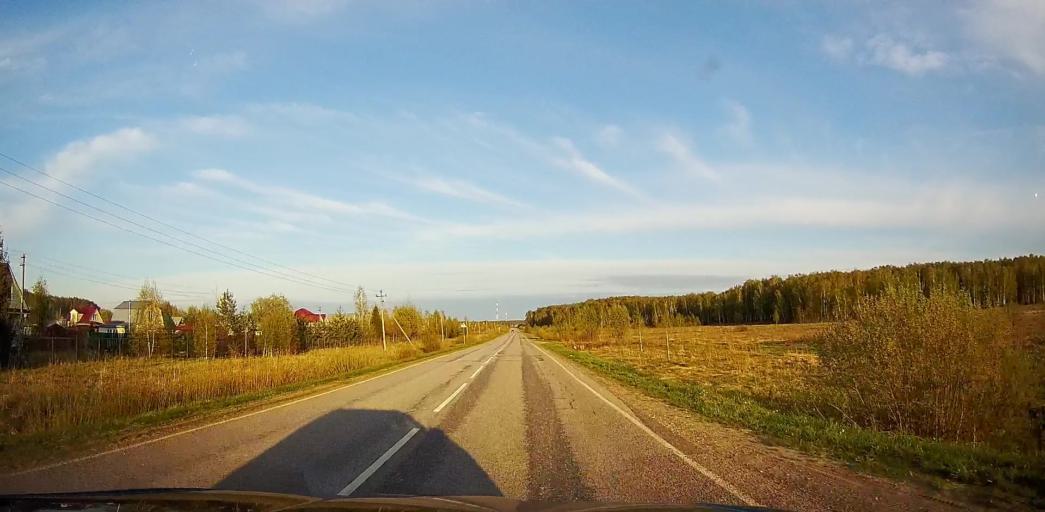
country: RU
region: Moskovskaya
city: Meshcherino
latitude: 55.2404
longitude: 38.3384
